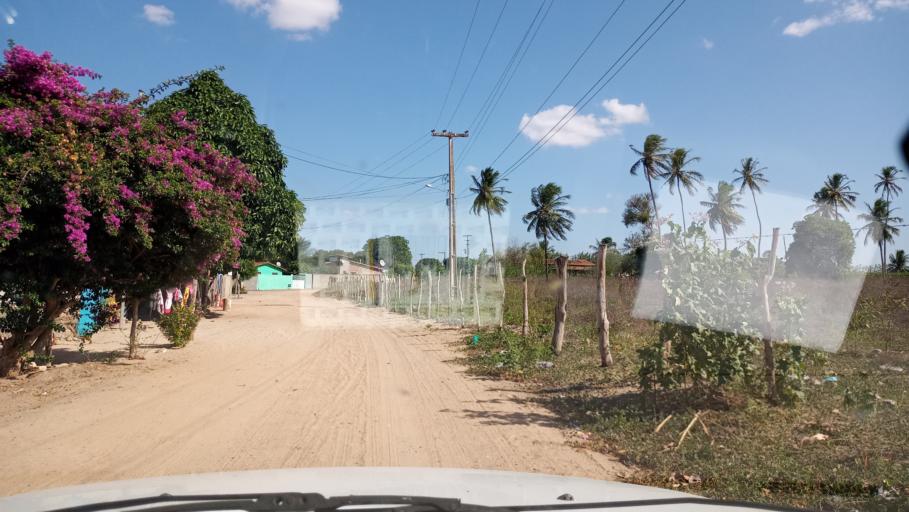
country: BR
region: Rio Grande do Norte
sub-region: Brejinho
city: Brejinho
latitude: -6.1726
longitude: -35.4684
